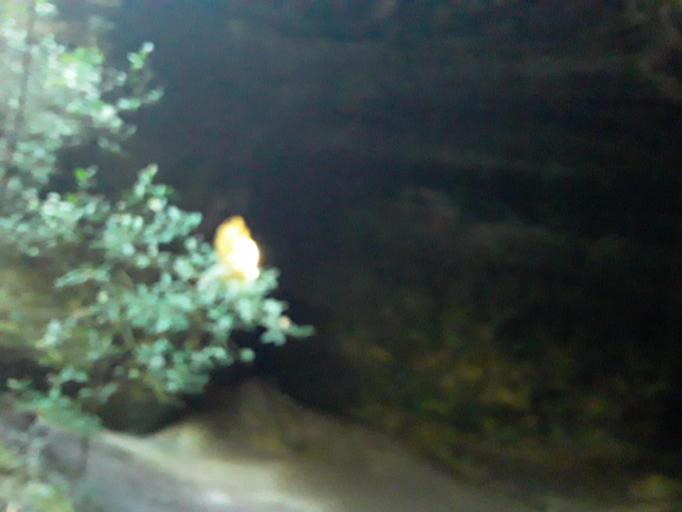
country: BR
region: Minas Gerais
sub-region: Lima Duarte
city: Lima Duarte
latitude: -21.6785
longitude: -43.8828
